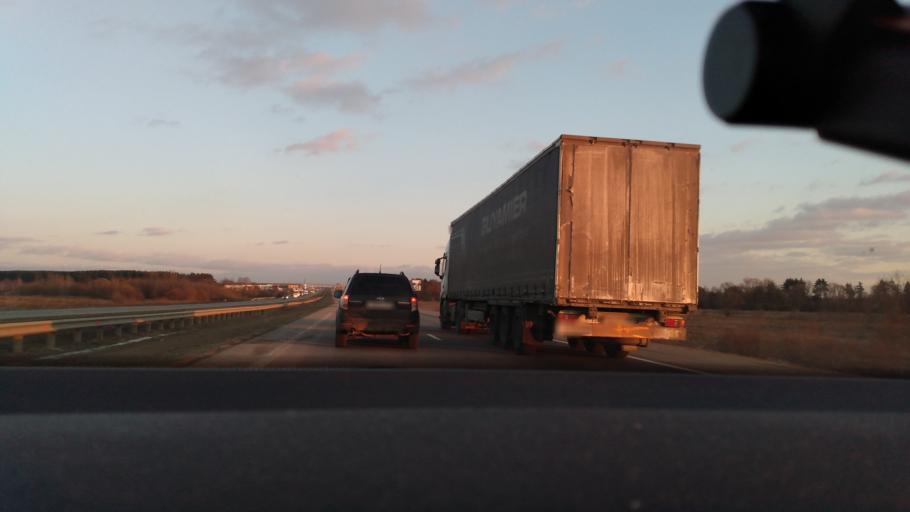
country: RU
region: Moskovskaya
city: Kolomna
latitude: 55.1252
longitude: 38.7970
